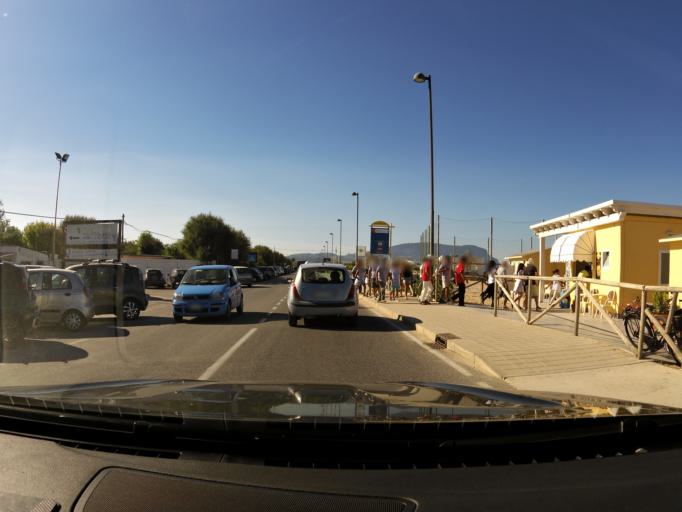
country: IT
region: The Marches
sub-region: Provincia di Ancona
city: Loreto Stazione
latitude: 43.4663
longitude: 13.6458
